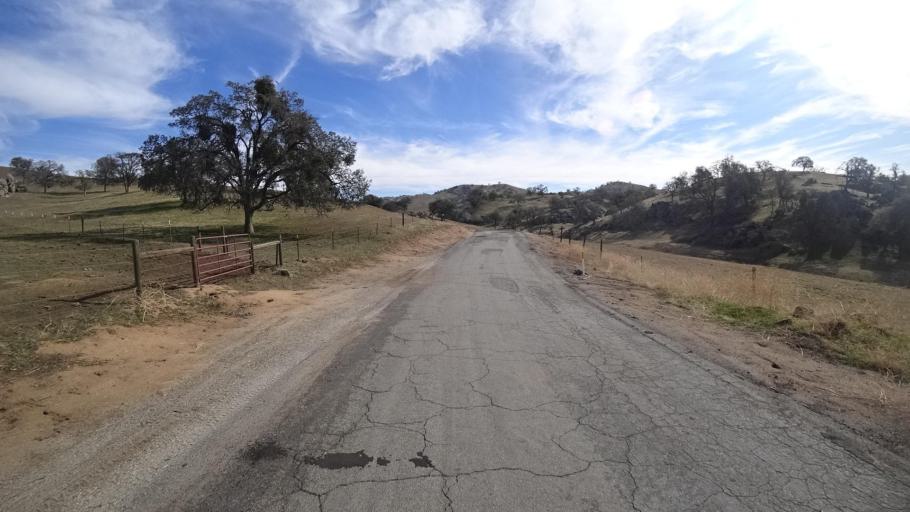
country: US
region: California
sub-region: Kern County
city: Oildale
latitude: 35.6148
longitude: -118.8458
